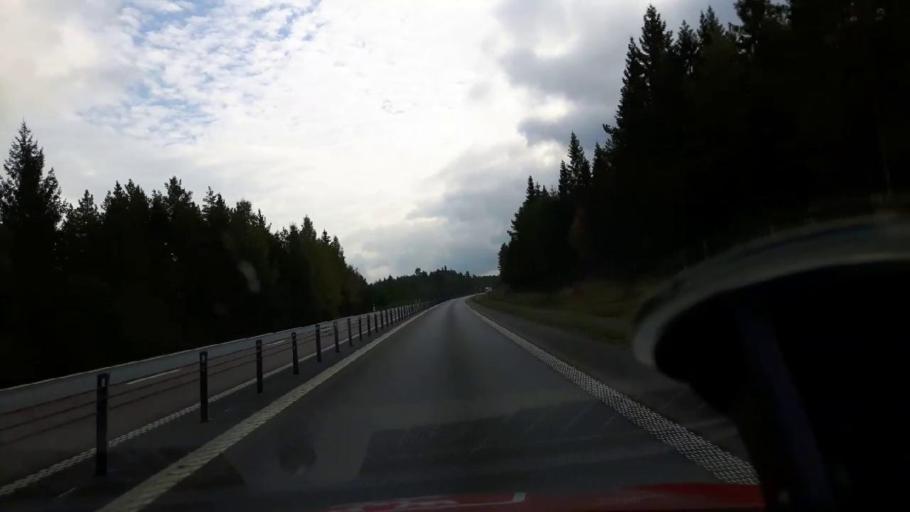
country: SE
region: Gaevleborg
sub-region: Gavle Kommun
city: Norrsundet
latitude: 60.8887
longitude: 17.0391
